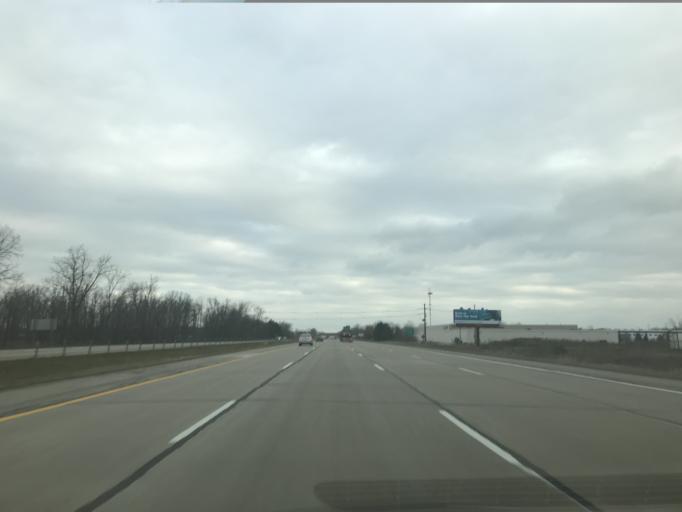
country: US
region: Michigan
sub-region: Eaton County
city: Dimondale
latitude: 42.7027
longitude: -84.6696
